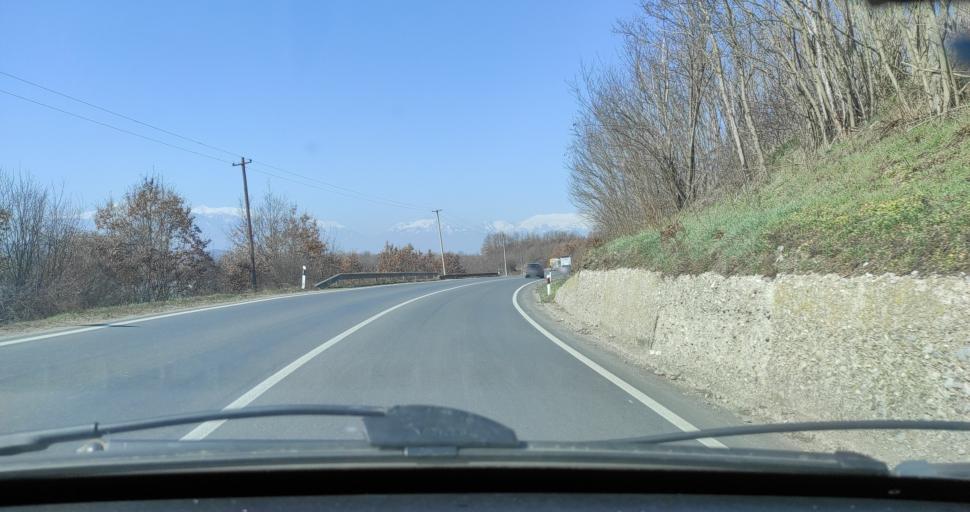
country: XK
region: Pec
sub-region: Komuna e Klines
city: Klina
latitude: 42.5961
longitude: 20.5356
